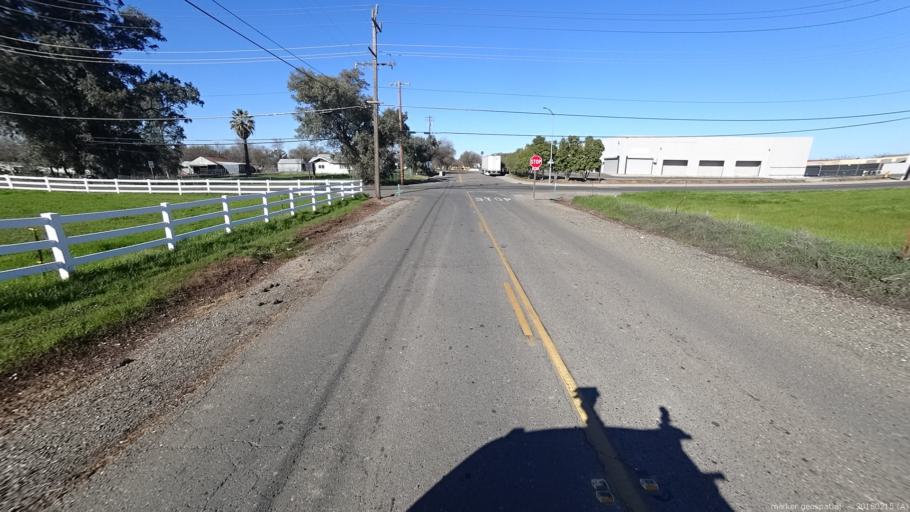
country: US
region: California
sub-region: Sacramento County
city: Rio Linda
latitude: 38.6975
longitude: -121.4106
